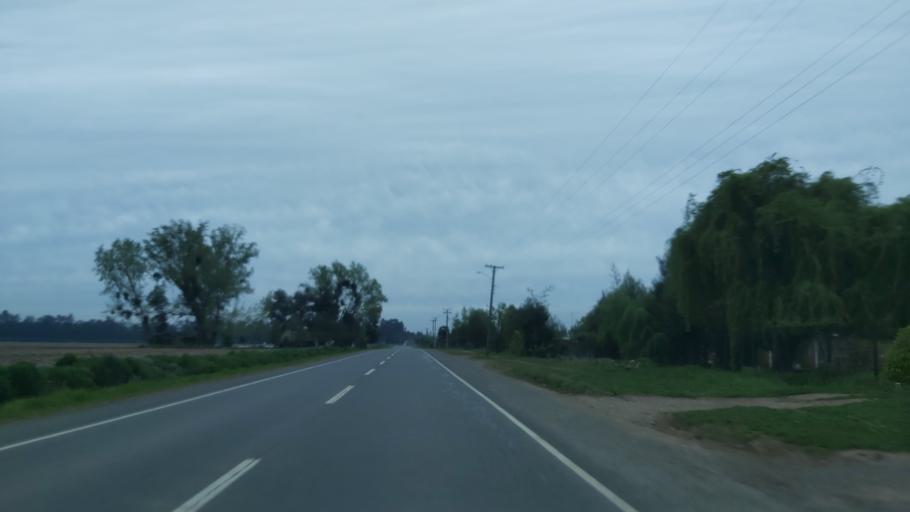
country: CL
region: Maule
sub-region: Provincia de Linares
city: Linares
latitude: -35.7743
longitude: -71.5161
